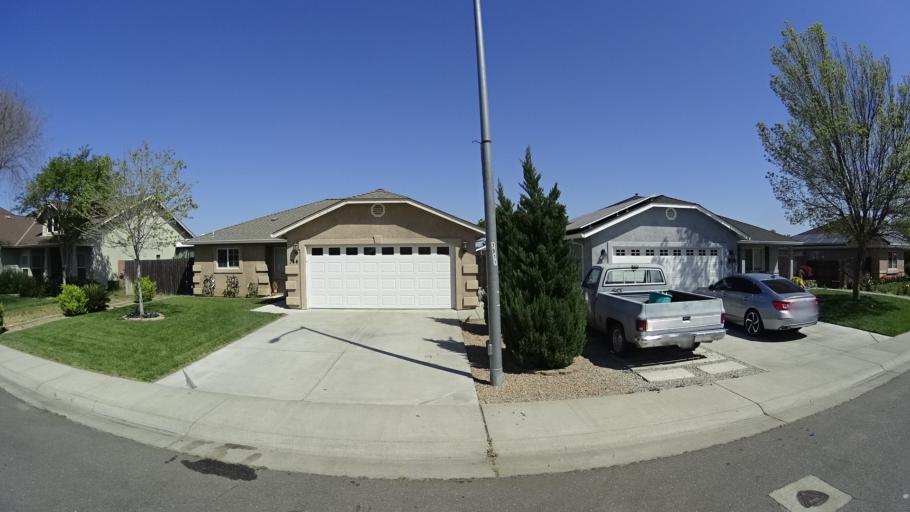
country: US
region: California
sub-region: Glenn County
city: Orland
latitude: 39.7590
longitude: -122.2000
